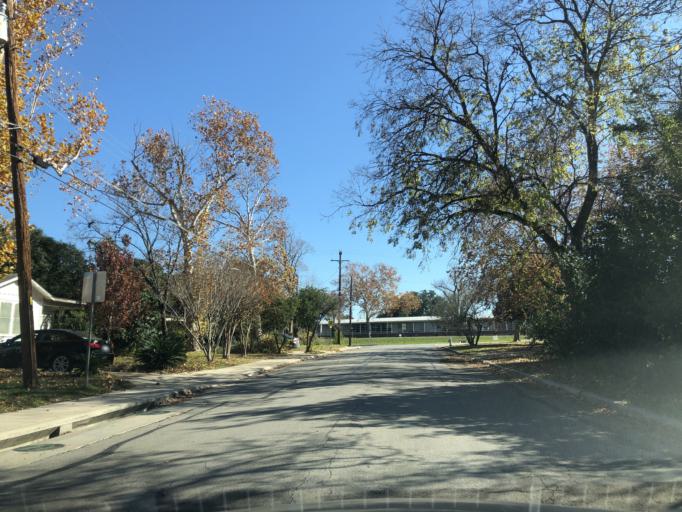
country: US
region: Texas
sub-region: Travis County
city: Austin
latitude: 30.3390
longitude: -97.7417
